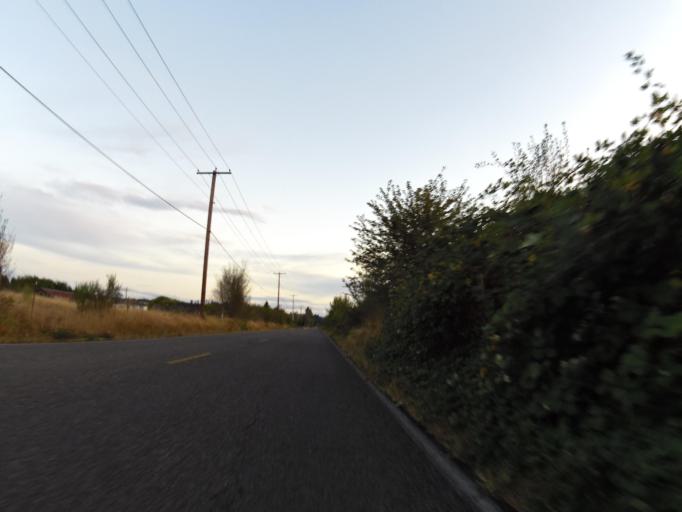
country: US
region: Washington
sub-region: Thurston County
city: Tenino
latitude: 46.8281
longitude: -122.8613
